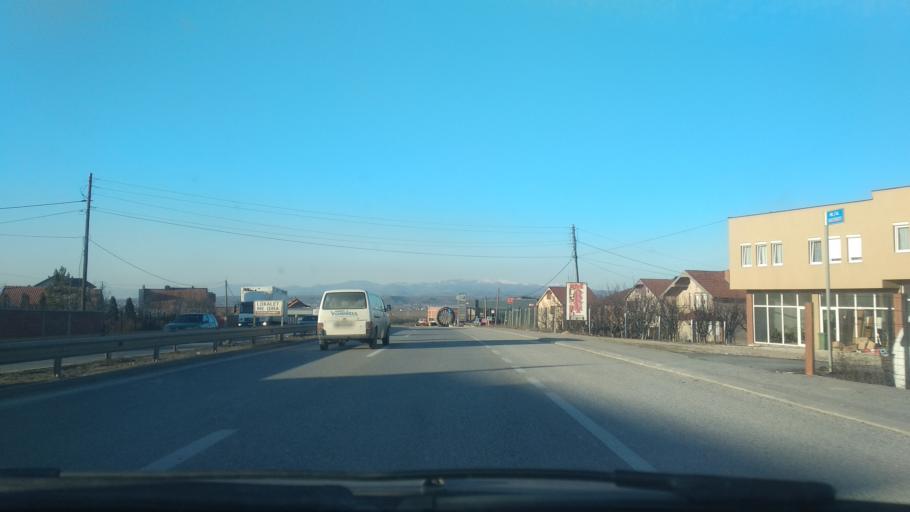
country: XK
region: Pristina
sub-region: Kosovo Polje
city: Kosovo Polje
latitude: 42.6917
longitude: 21.1180
